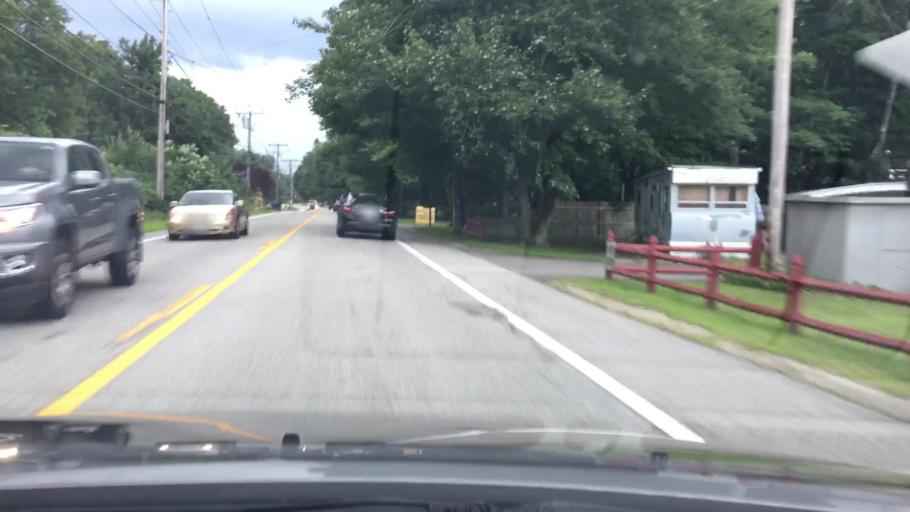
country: US
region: Rhode Island
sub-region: Providence County
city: Cumberland
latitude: 41.9948
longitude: -71.4152
